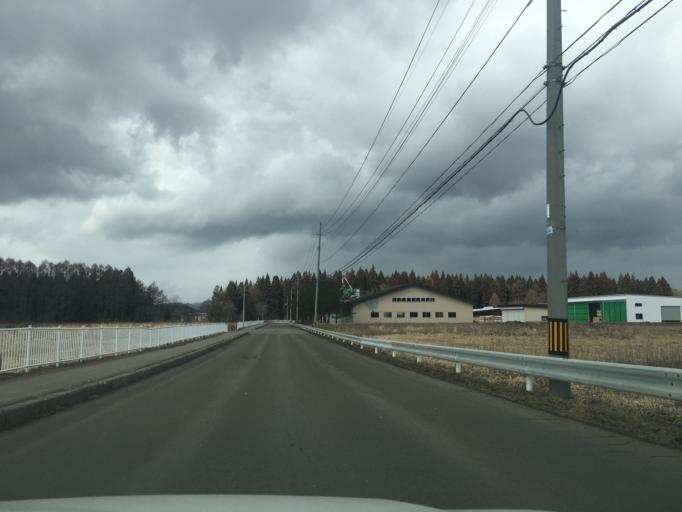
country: JP
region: Akita
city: Takanosu
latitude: 40.1840
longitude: 140.3413
